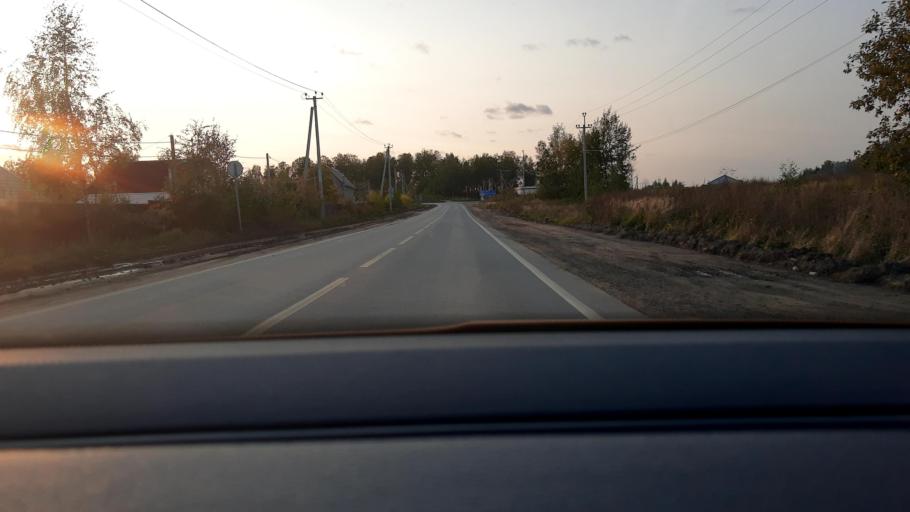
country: RU
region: Moskovskaya
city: Lobnya
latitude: 55.9987
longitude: 37.4045
